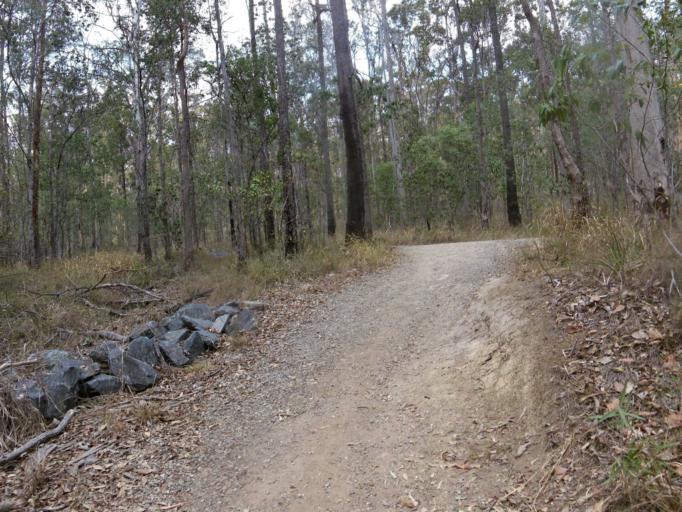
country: AU
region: Queensland
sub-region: Logan
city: Springwood
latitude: -27.6064
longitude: 153.1537
